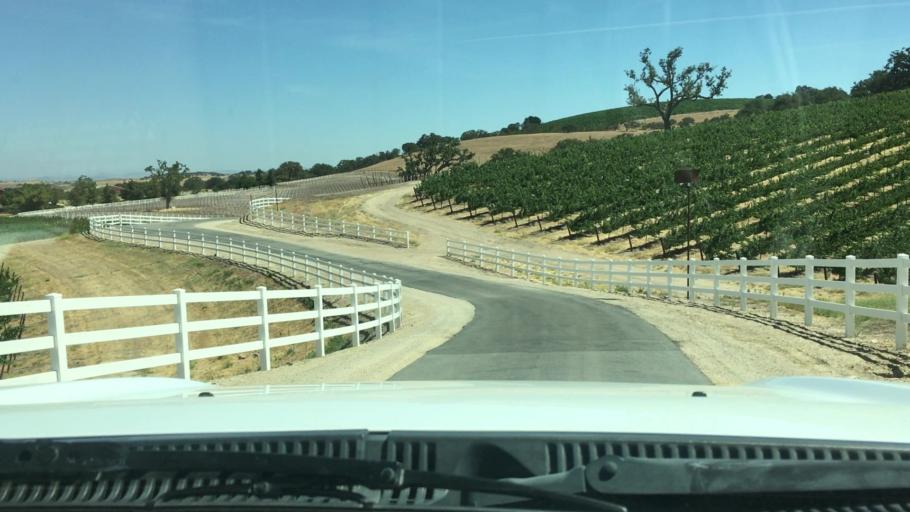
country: US
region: California
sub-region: San Luis Obispo County
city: Paso Robles
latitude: 35.5813
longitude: -120.6046
